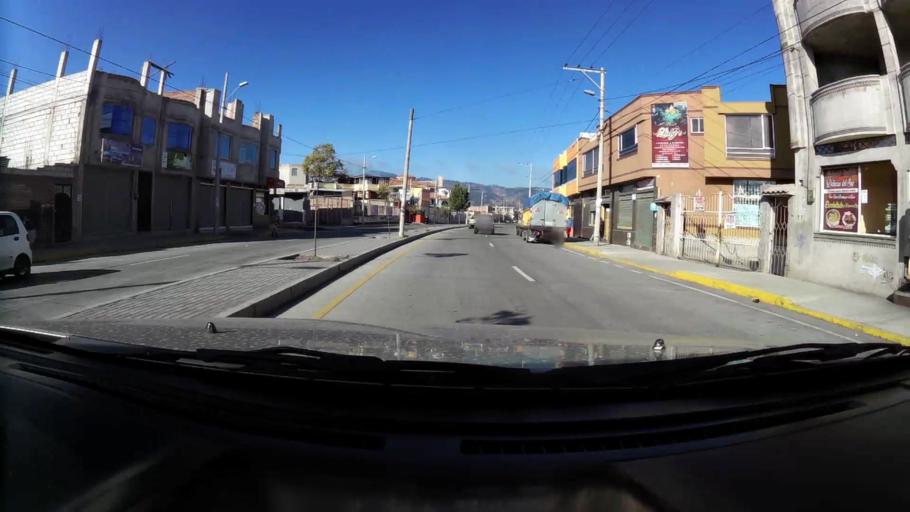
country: EC
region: Chimborazo
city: Riobamba
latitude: -1.6899
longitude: -78.6328
